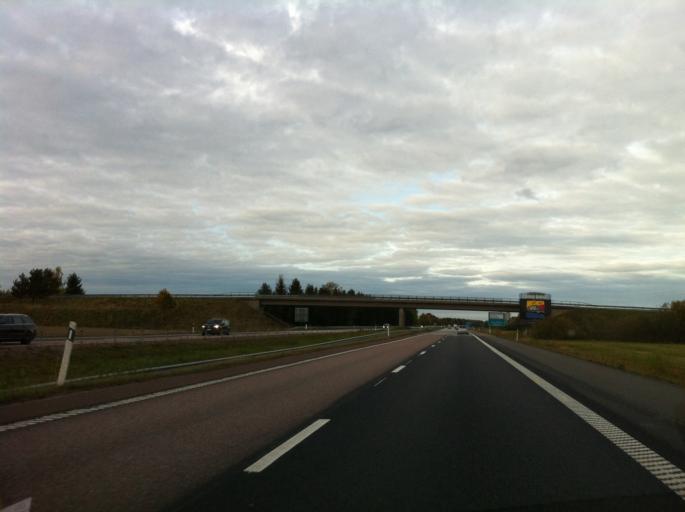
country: SE
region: OErebro
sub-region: Kumla Kommun
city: Kumla
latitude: 59.1787
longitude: 15.1200
